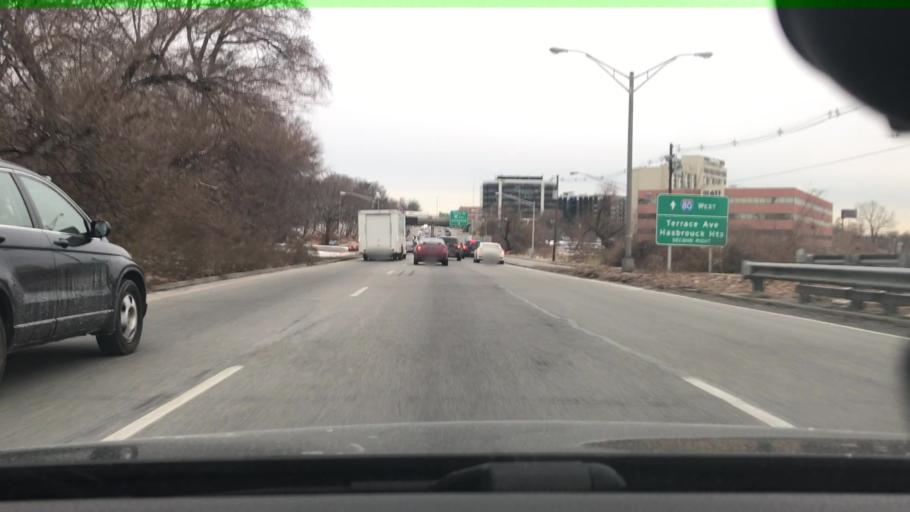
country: US
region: New Jersey
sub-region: Bergen County
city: Hasbrouck Heights
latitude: 40.8674
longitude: -74.0632
